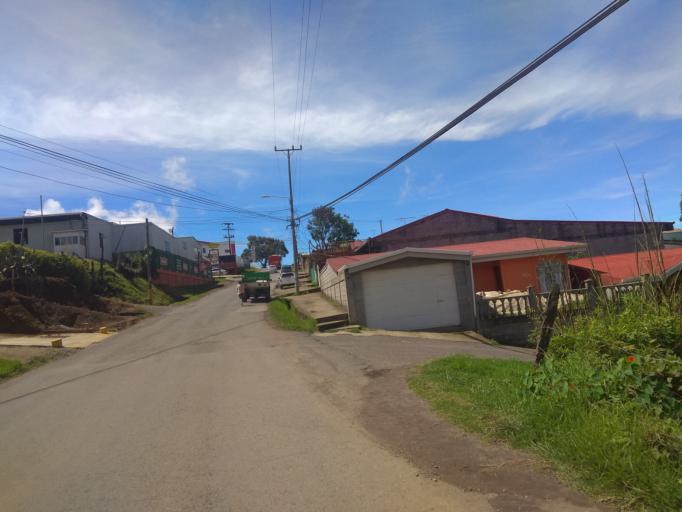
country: CR
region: Cartago
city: Cot
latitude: 9.9138
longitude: -83.8889
